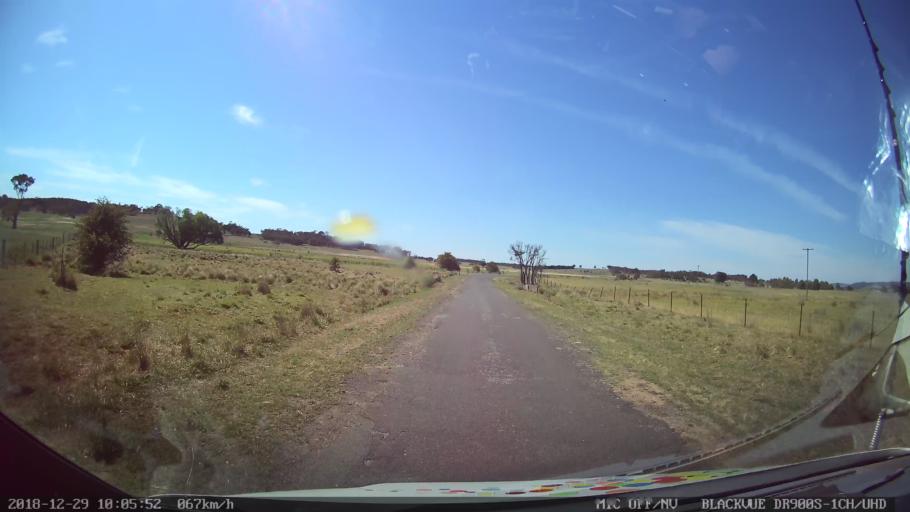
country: AU
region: New South Wales
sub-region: Goulburn Mulwaree
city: Goulburn
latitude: -34.8374
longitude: 149.4542
